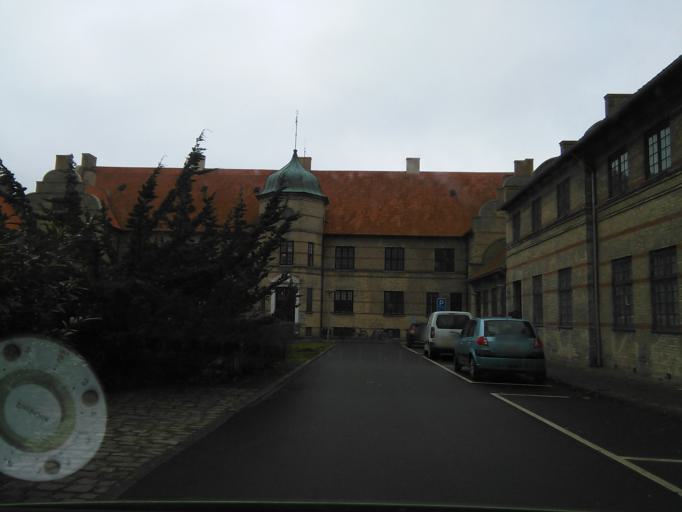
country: DK
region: Central Jutland
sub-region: Arhus Kommune
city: Arhus
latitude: 56.1859
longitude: 10.2316
